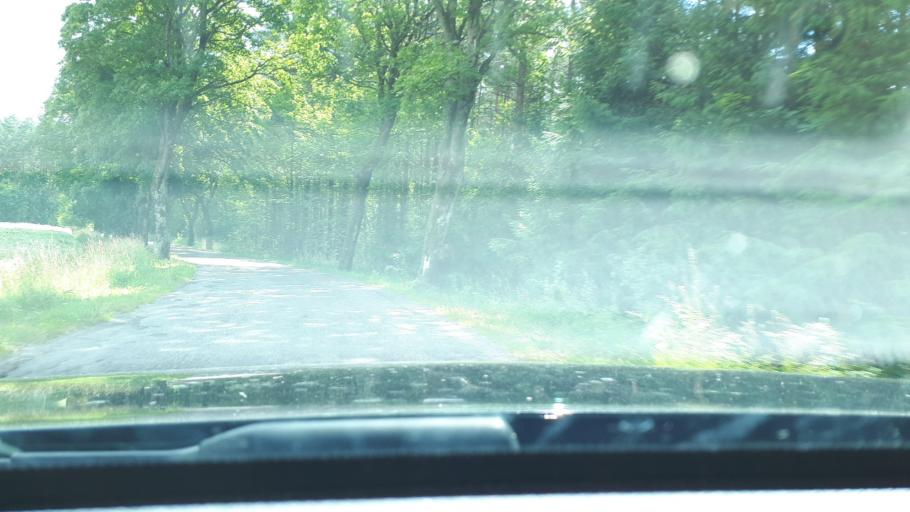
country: PL
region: Warmian-Masurian Voivodeship
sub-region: Powiat olsztynski
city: Olsztynek
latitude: 53.6101
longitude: 20.2553
